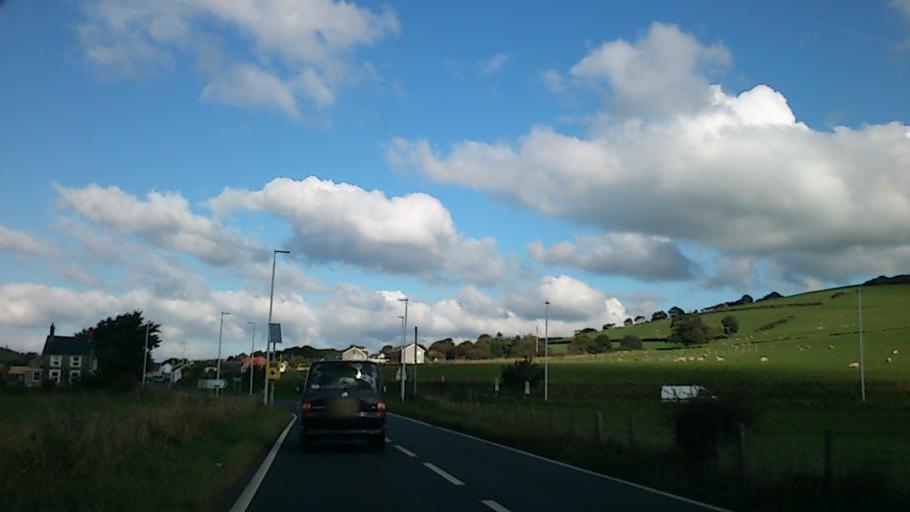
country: GB
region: Wales
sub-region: County of Ceredigion
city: Bow Street
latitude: 52.4383
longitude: -4.0298
